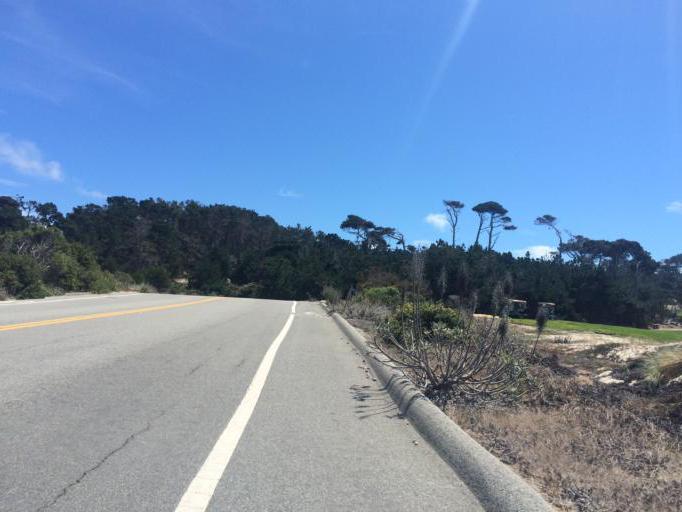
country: US
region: California
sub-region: Monterey County
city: Del Monte Forest
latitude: 36.5863
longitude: -121.9620
